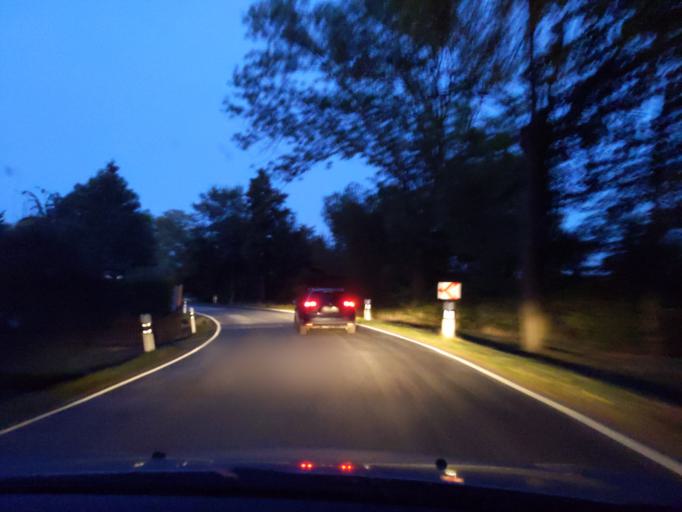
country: DE
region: Saxony
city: Malschwitz
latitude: 51.2618
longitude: 14.5249
